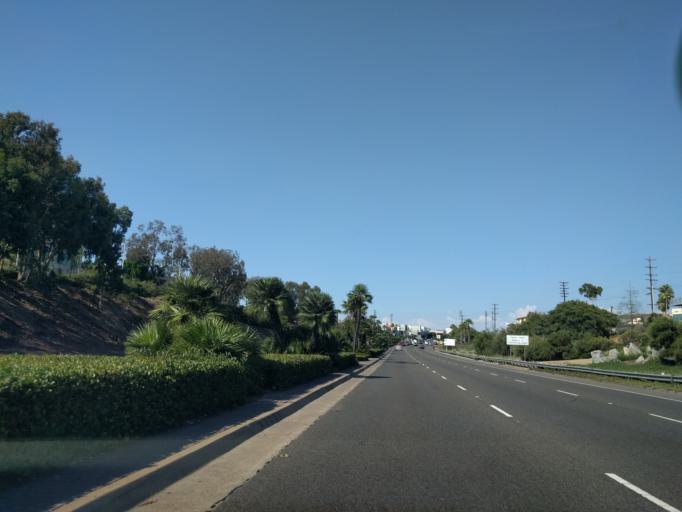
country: US
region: California
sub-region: Orange County
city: Newport Beach
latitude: 33.6281
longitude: -117.9270
